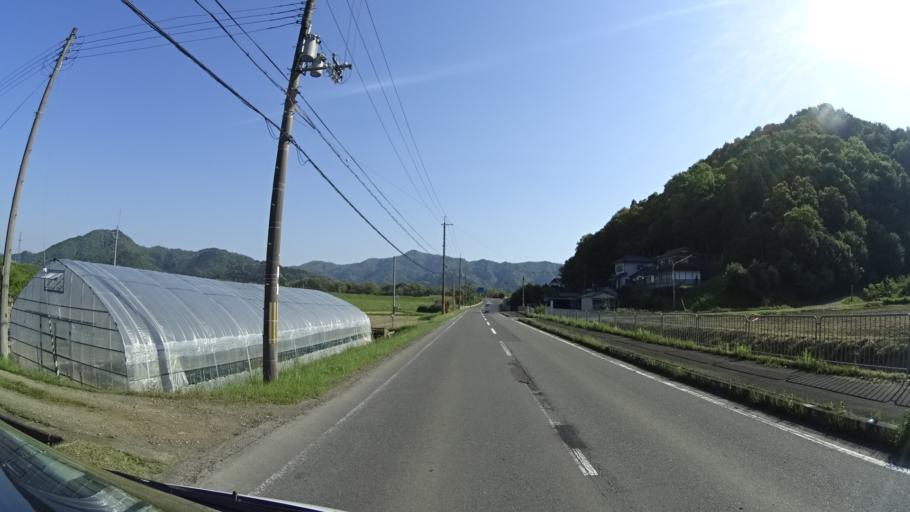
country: JP
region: Kyoto
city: Ayabe
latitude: 35.3138
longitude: 135.2087
